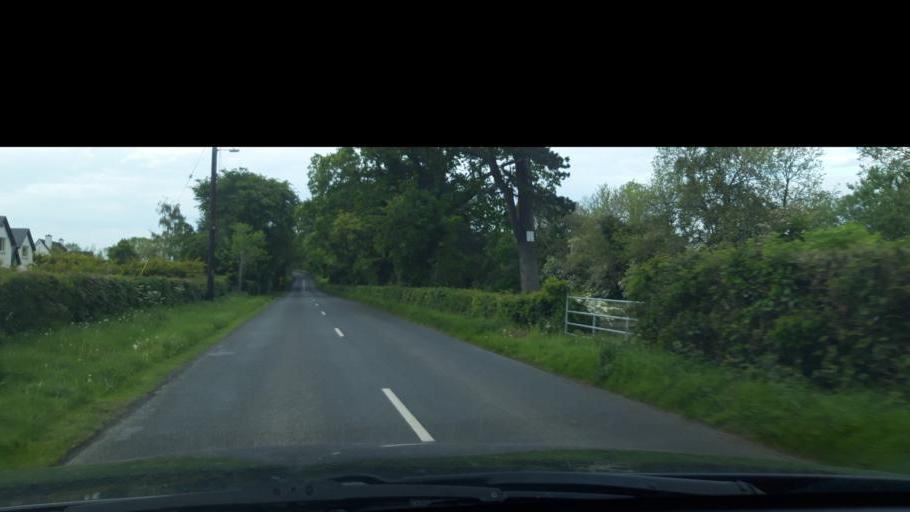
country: IE
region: Leinster
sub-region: Kildare
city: Celbridge
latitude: 53.3045
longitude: -6.5585
